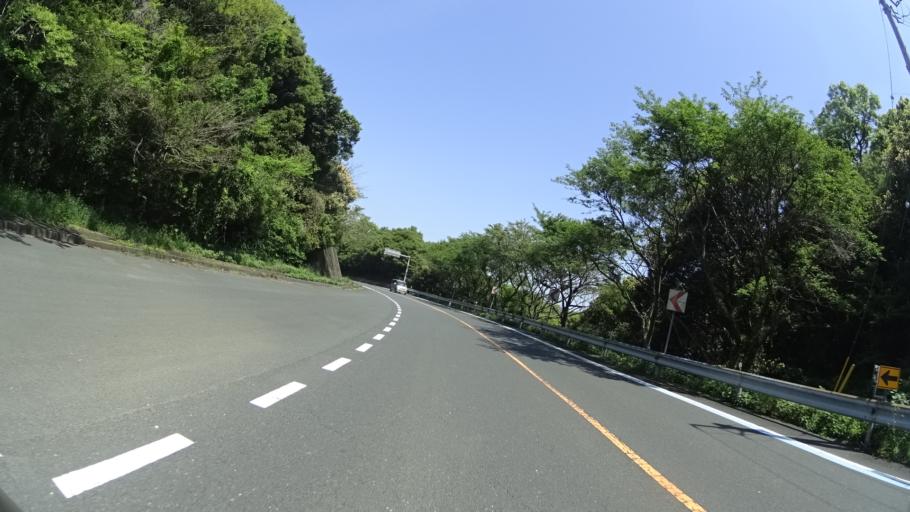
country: JP
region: Ehime
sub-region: Nishiuwa-gun
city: Ikata-cho
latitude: 33.4576
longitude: 132.2745
